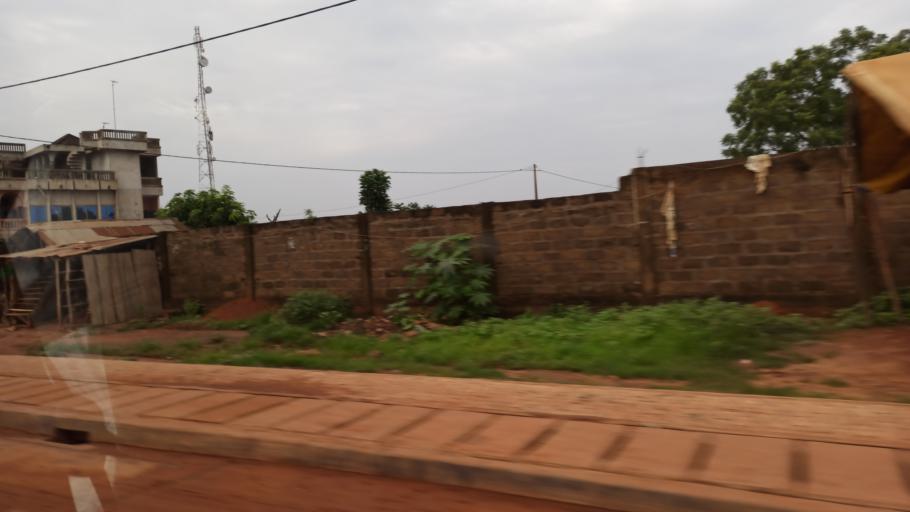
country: BJ
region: Queme
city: Porto-Novo
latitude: 6.5592
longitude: 2.5888
